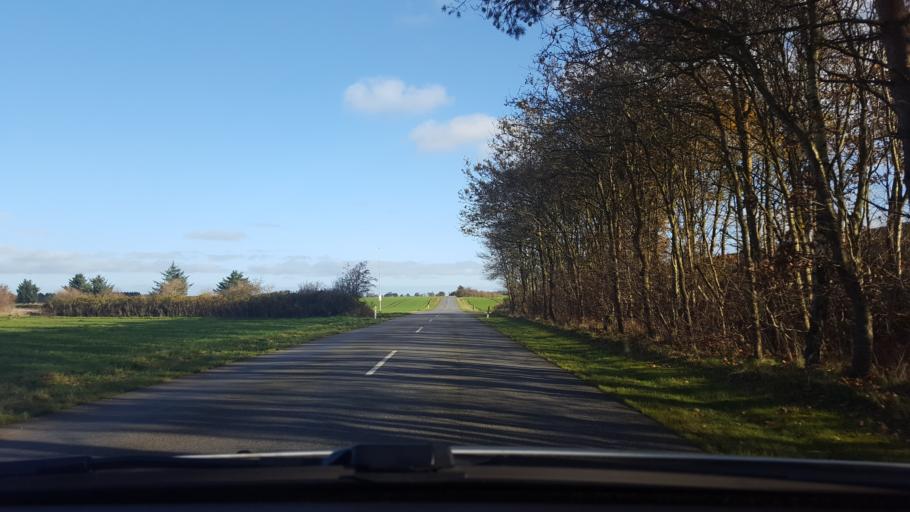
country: DK
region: North Denmark
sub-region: Morso Kommune
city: Nykobing Mors
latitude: 56.7425
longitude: 8.8775
